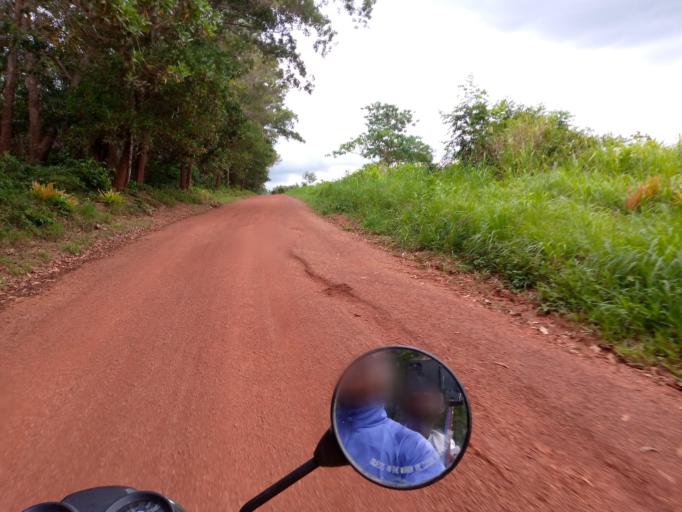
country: SL
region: Northern Province
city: Mange
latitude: 8.8982
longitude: -12.7204
